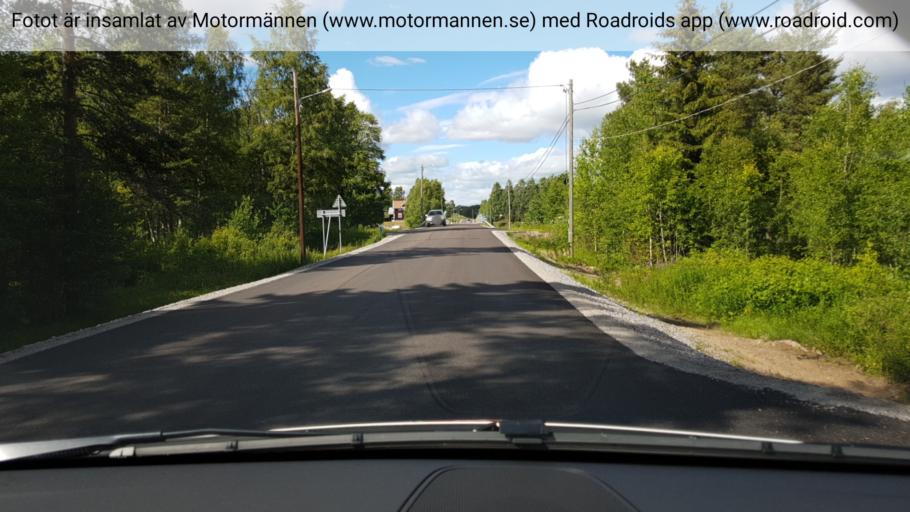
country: SE
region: Jaemtland
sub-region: Harjedalens Kommun
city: Sveg
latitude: 61.8461
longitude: 14.0690
